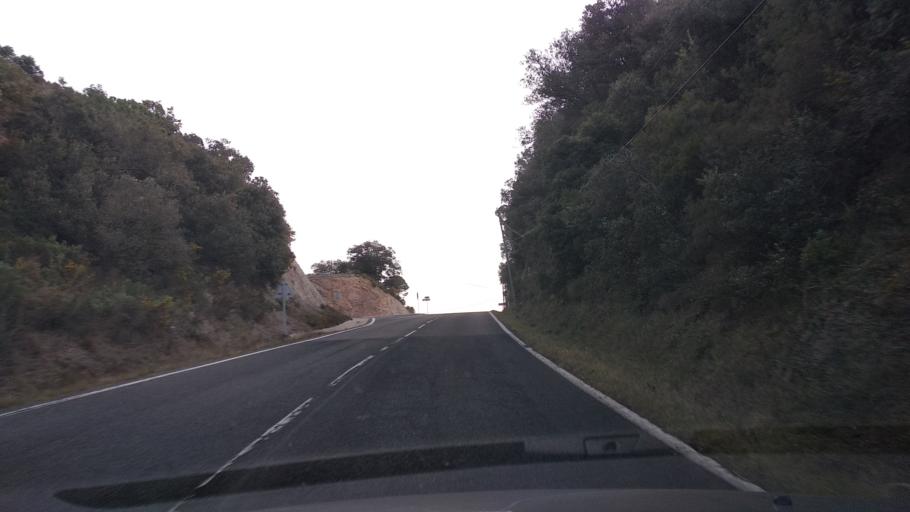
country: ES
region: Catalonia
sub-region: Provincia de Tarragona
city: Alforja
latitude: 41.2223
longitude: 0.9327
